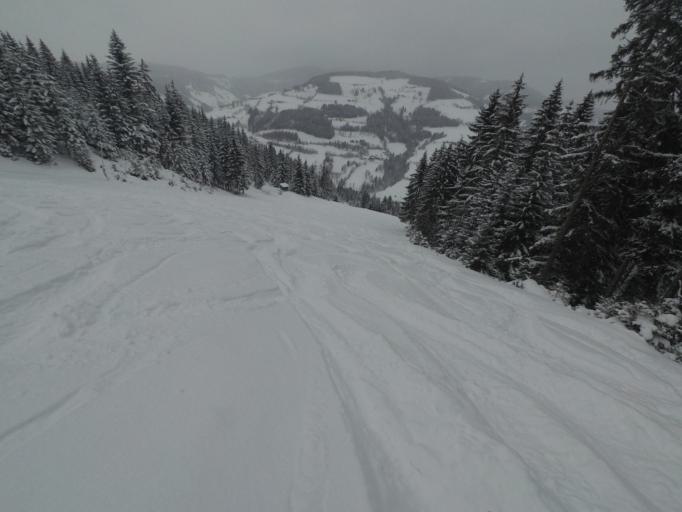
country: AT
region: Salzburg
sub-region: Politischer Bezirk Sankt Johann im Pongau
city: Wagrain
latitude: 47.3252
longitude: 13.2908
